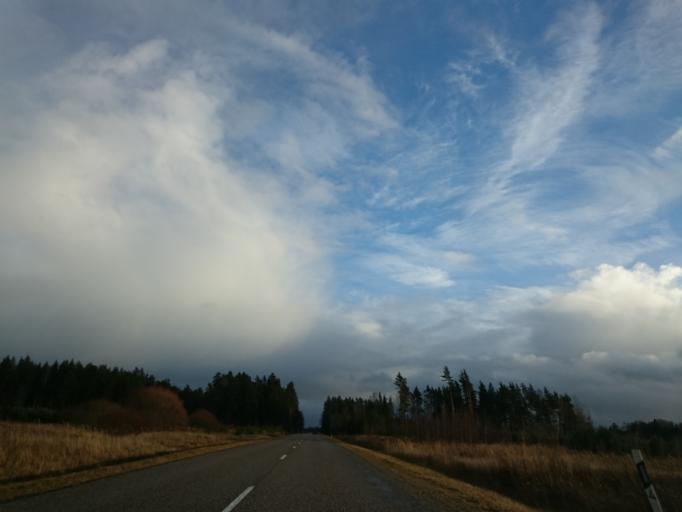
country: LV
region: Skrunda
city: Skrunda
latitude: 56.6807
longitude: 21.9529
